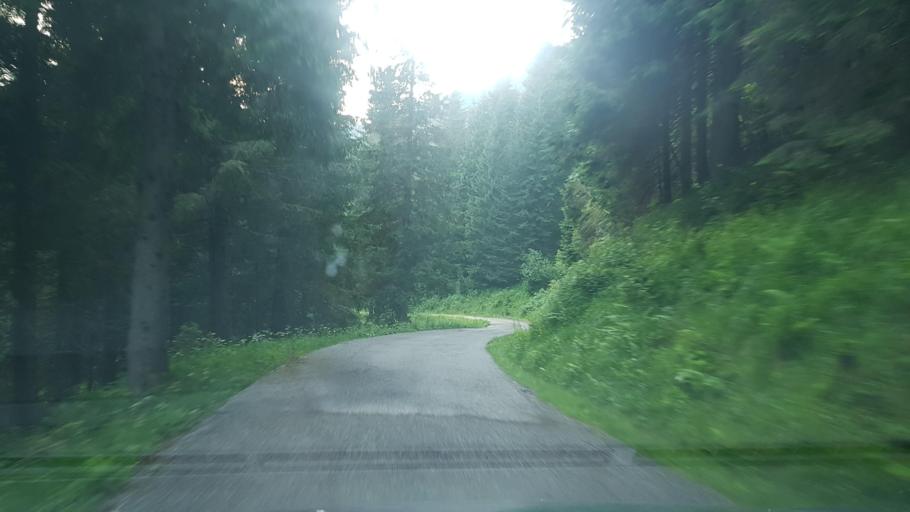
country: IT
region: Friuli Venezia Giulia
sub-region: Provincia di Udine
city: Paularo
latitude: 46.5757
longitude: 13.1556
